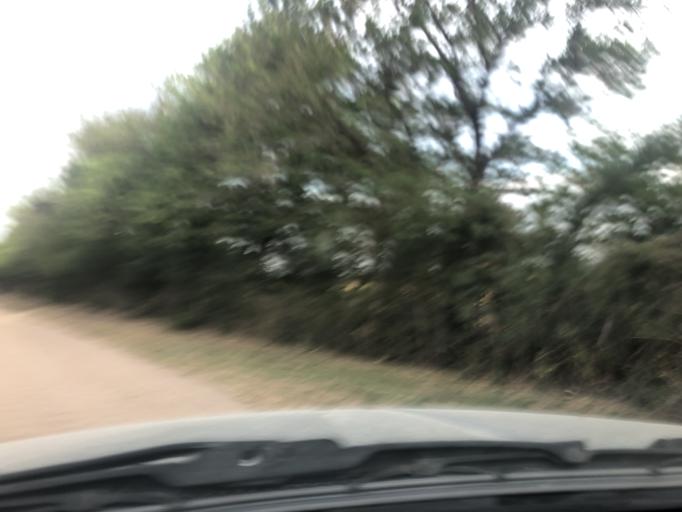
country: AR
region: Cordoba
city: La Granja
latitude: -31.0174
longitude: -64.2511
